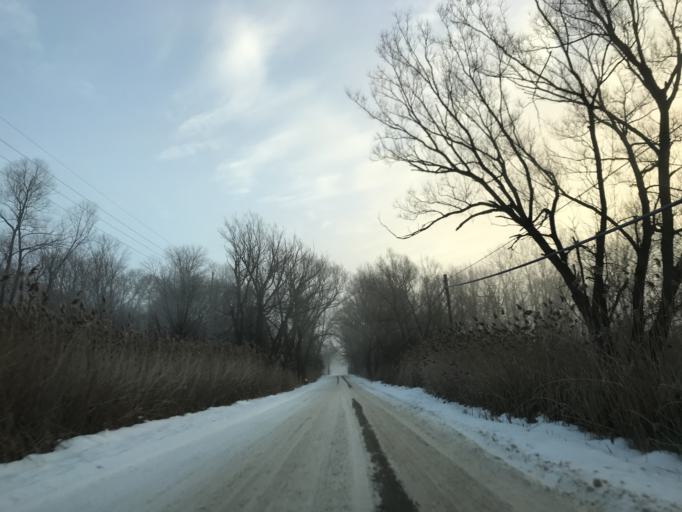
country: US
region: Michigan
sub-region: Oakland County
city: Wixom
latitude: 42.4922
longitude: -83.5787
